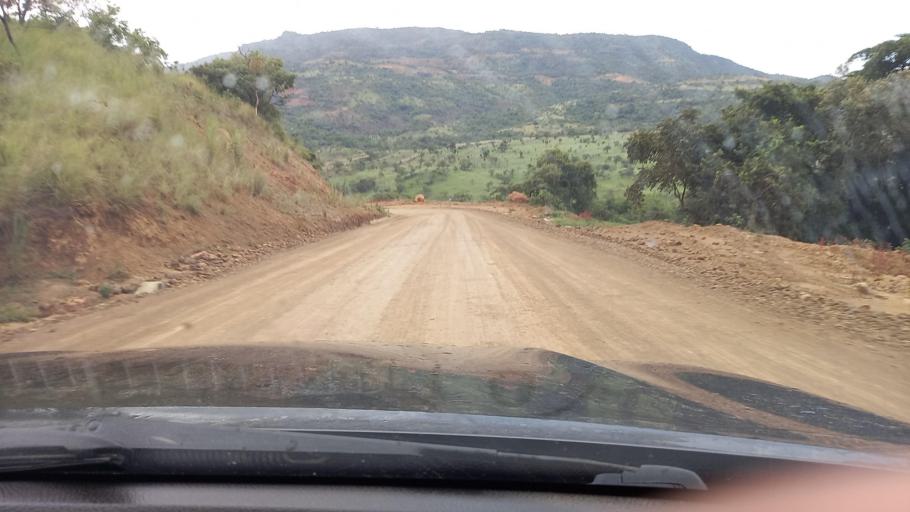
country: ET
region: Southern Nations, Nationalities, and People's Region
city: Mizan Teferi
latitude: 6.1907
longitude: 35.6802
